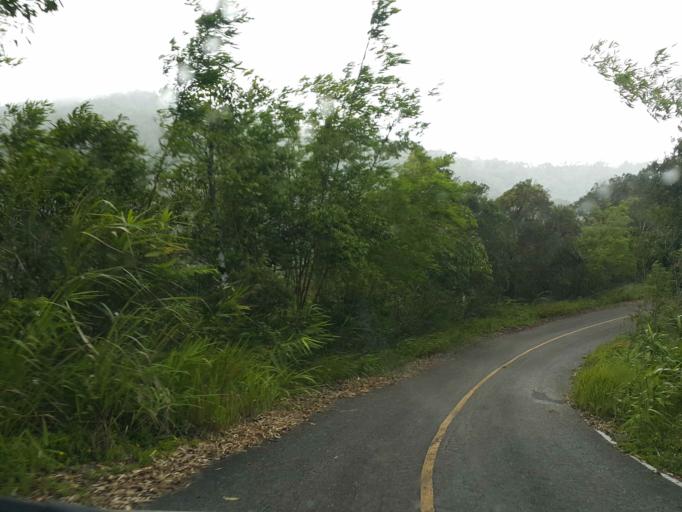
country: TH
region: Tak
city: Tak
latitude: 16.7885
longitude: 98.9219
